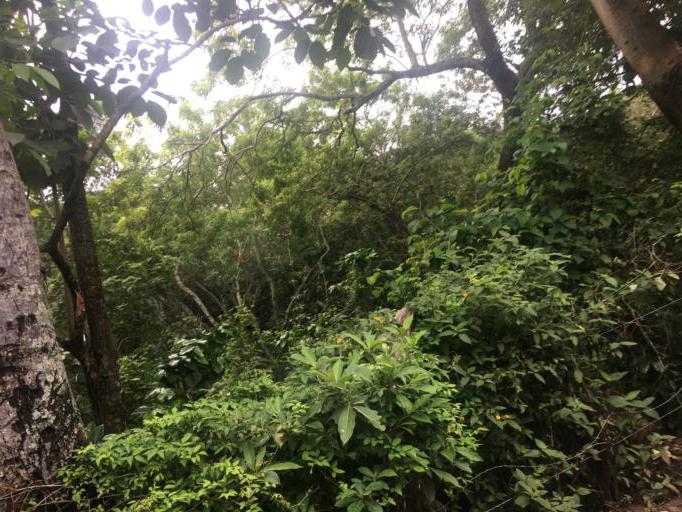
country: GT
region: Escuintla
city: San Vicente Pacaya
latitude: 14.3226
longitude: -90.5607
